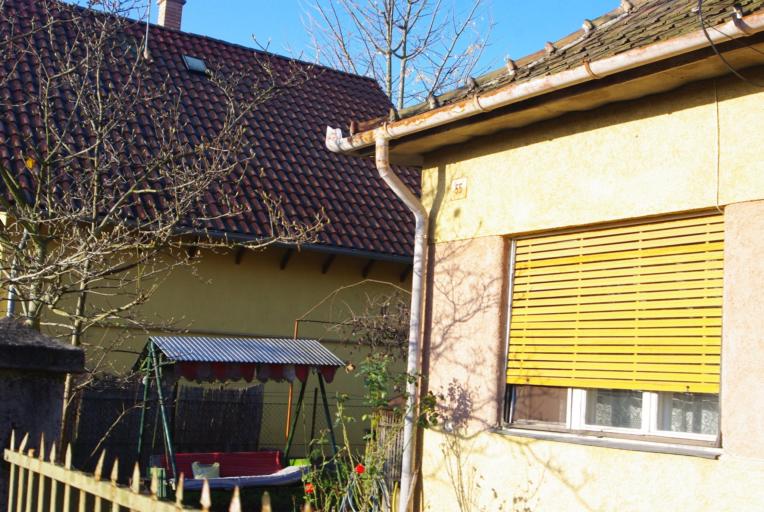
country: HU
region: Pest
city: God
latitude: 47.6809
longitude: 19.1407
